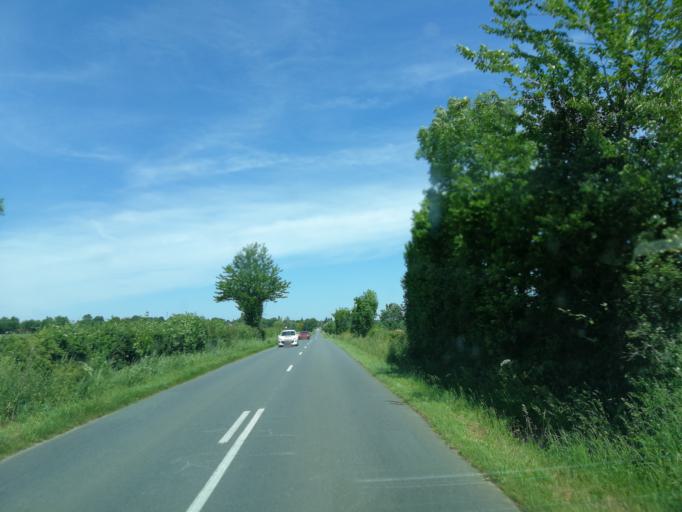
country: FR
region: Poitou-Charentes
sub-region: Departement des Deux-Sevres
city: La Foret-sur-Sevre
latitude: 46.7866
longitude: -0.6154
